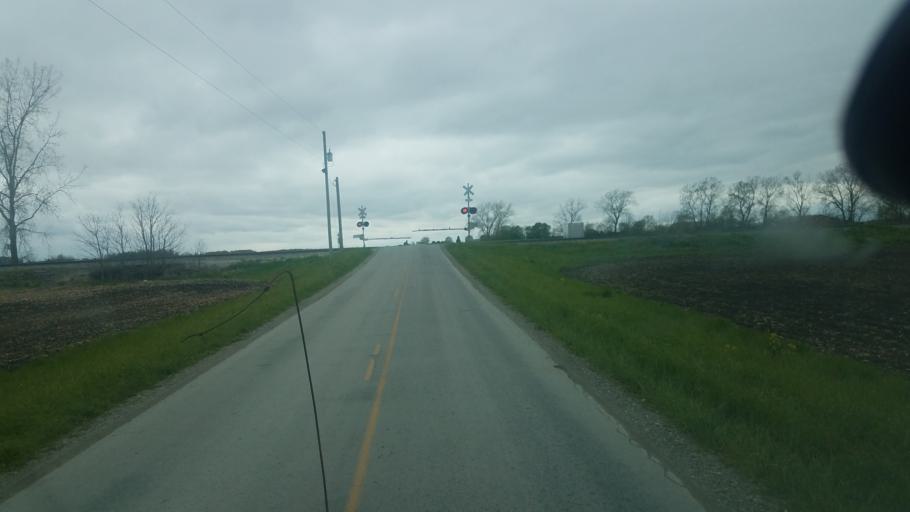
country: US
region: Ohio
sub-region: Wyandot County
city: Upper Sandusky
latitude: 40.8021
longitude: -83.2914
